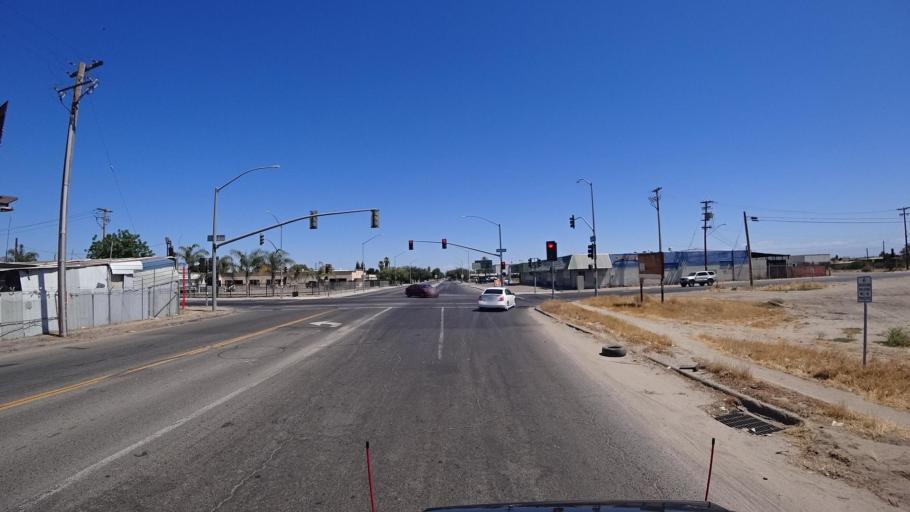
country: US
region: California
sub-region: Fresno County
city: Easton
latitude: 36.6920
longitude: -119.7907
